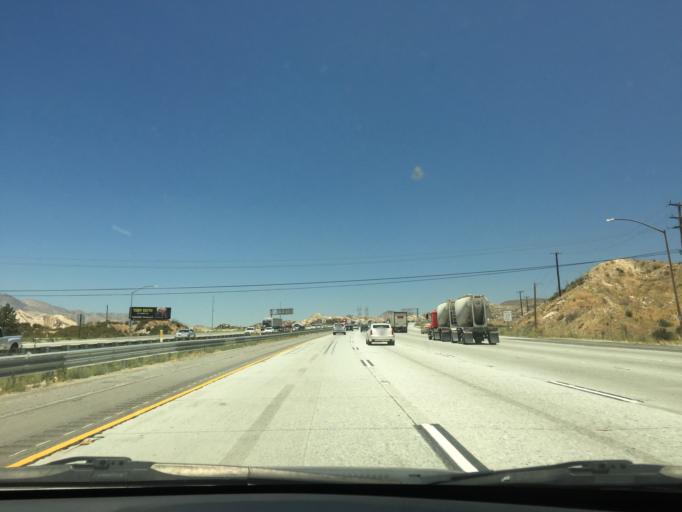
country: US
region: California
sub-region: San Bernardino County
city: Oak Hills
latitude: 34.3136
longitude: -117.4767
